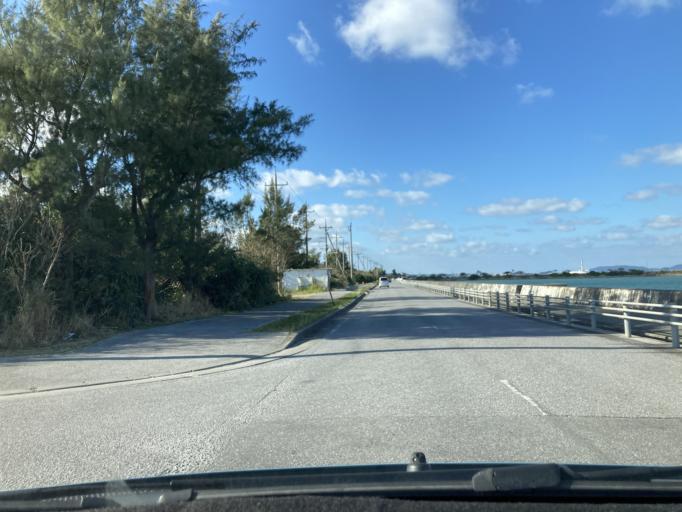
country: JP
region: Okinawa
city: Katsuren-haebaru
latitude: 26.3265
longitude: 127.9112
